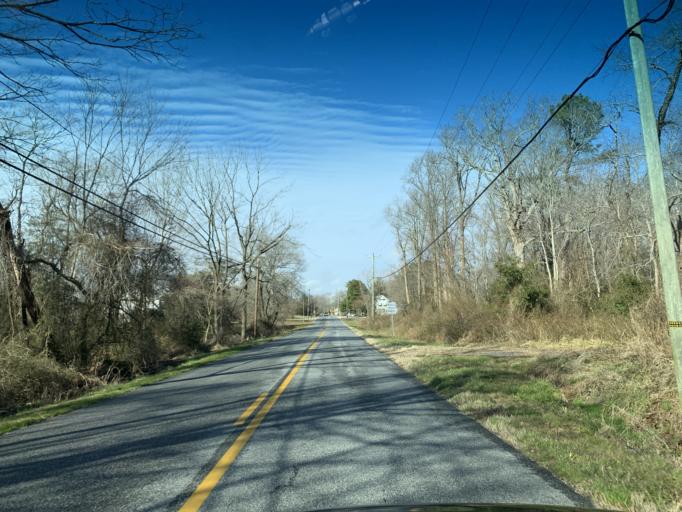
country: US
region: Delaware
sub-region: Sussex County
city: Selbyville
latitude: 38.4384
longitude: -75.1886
